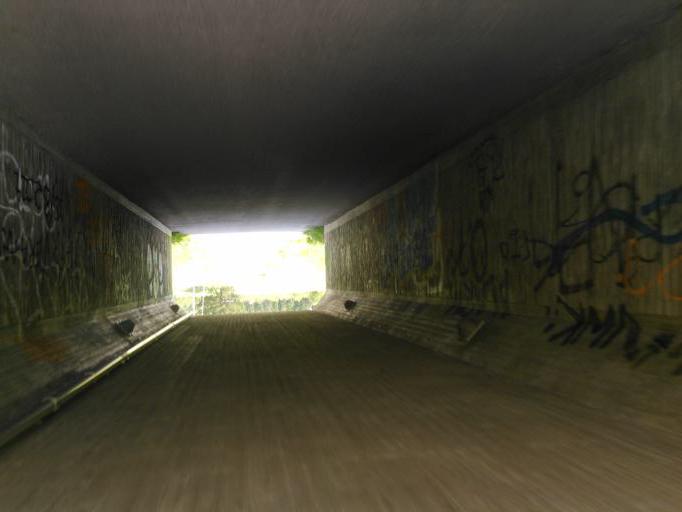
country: SE
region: Vaesterbotten
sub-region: Umea Kommun
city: Umea
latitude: 63.8371
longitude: 20.2717
